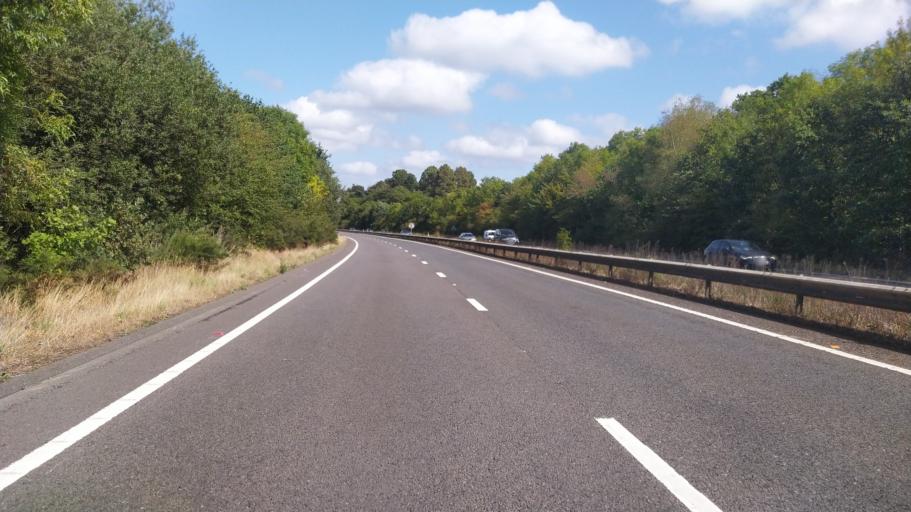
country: GB
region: England
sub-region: Hampshire
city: Liss
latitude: 51.0312
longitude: -0.9093
